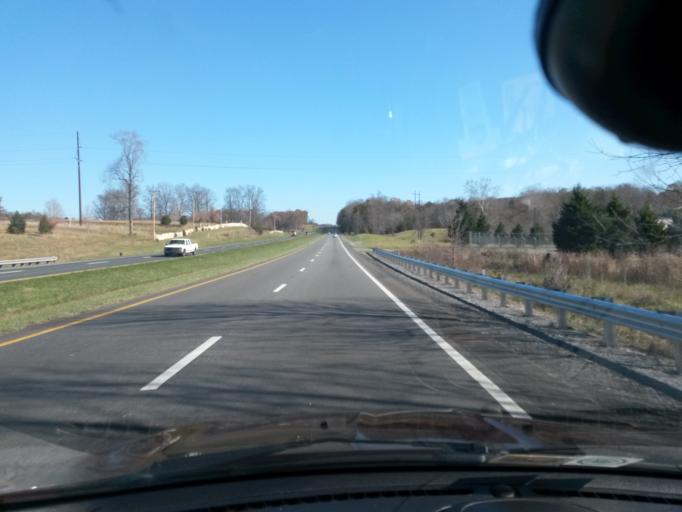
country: US
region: Virginia
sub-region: Campbell County
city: Timberlake
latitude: 37.3030
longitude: -79.3254
